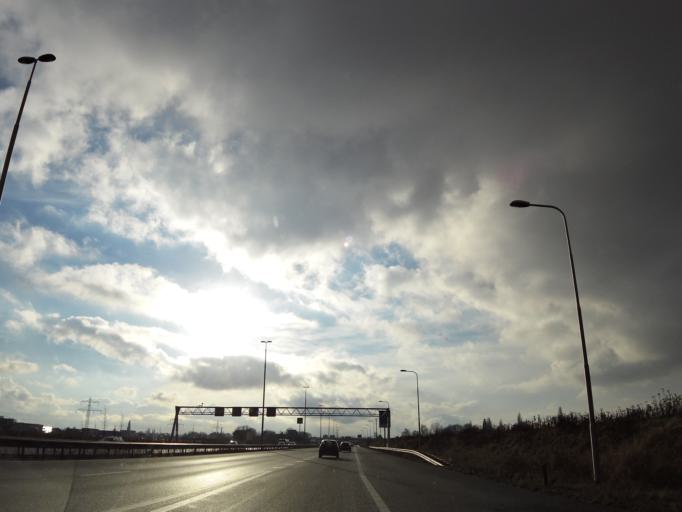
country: NL
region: Limburg
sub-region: Gemeente Maasgouw
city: Maasbracht
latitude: 51.1203
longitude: 5.8779
